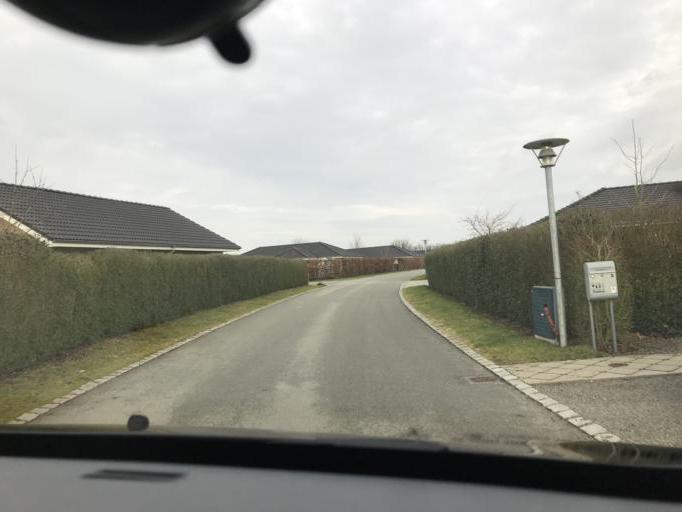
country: DK
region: South Denmark
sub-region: Faaborg-Midtfyn Kommune
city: Ringe
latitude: 55.2474
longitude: 10.4691
